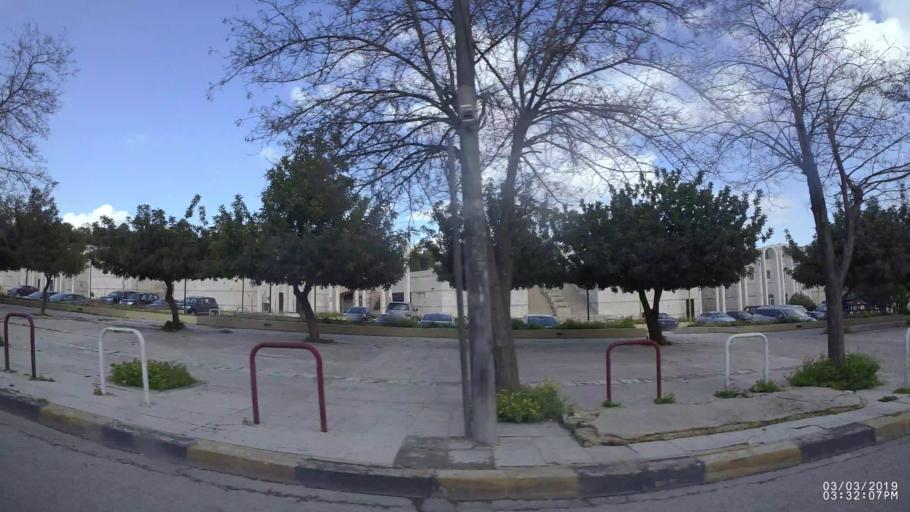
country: JO
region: Amman
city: Amman
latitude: 31.9683
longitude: 35.8867
